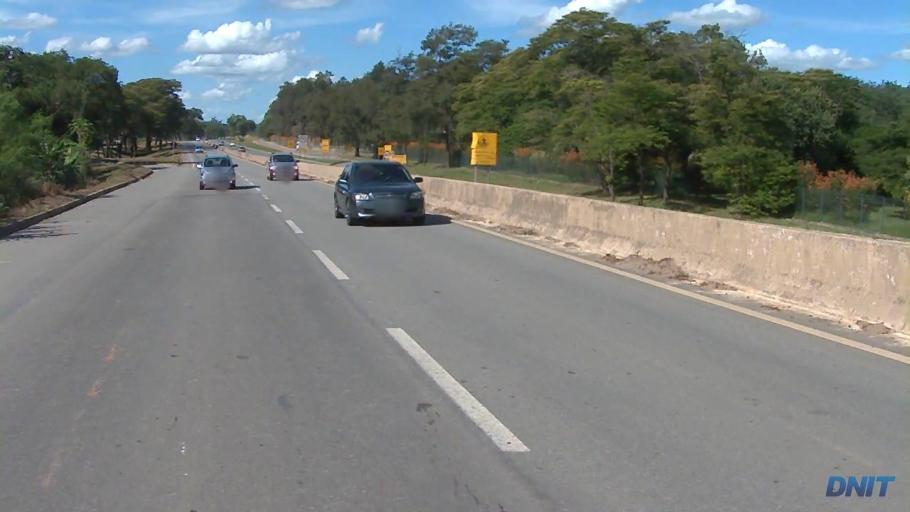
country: BR
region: Minas Gerais
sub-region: Ipaba
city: Ipaba
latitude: -19.3167
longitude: -42.4009
